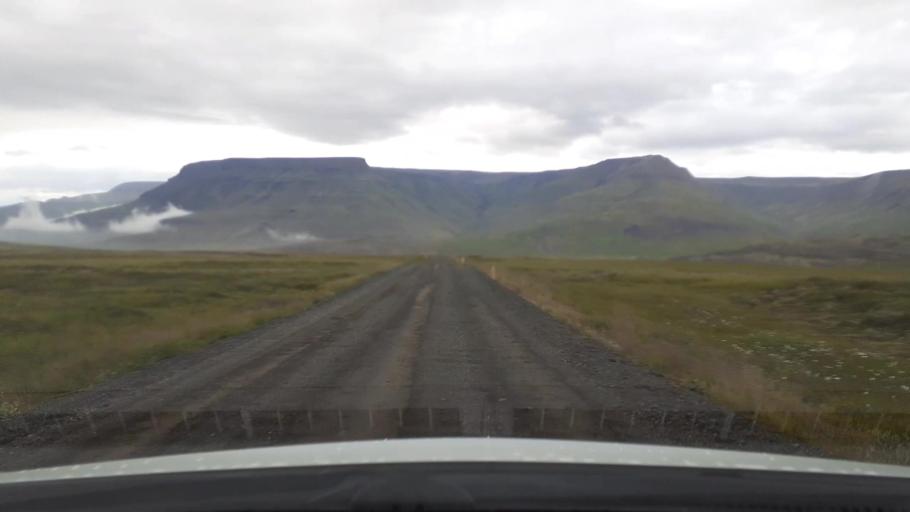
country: IS
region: Capital Region
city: Mosfellsbaer
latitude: 64.1937
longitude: -21.5435
